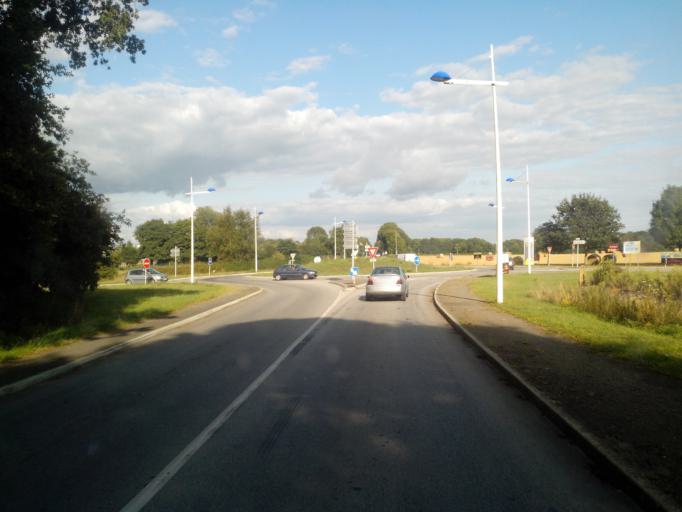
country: FR
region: Brittany
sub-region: Departement du Morbihan
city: Kervignac
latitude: 47.7969
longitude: -3.2394
